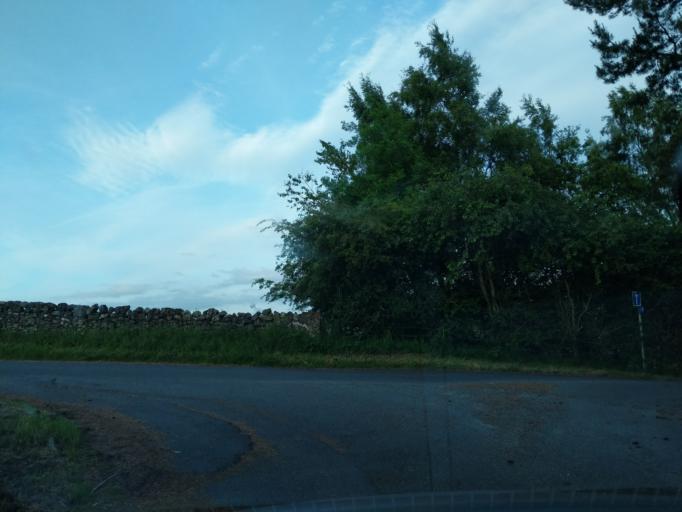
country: GB
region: Scotland
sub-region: Midlothian
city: Gorebridge
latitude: 55.7769
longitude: -3.1033
